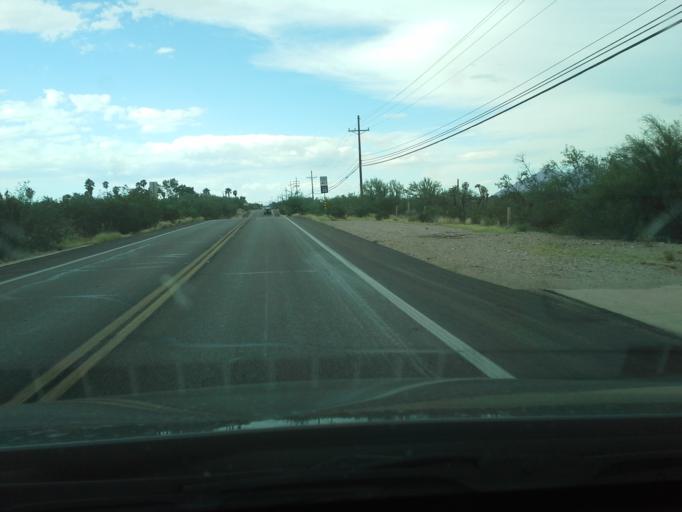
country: US
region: Arizona
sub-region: Pima County
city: South Tucson
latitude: 32.2125
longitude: -111.0203
